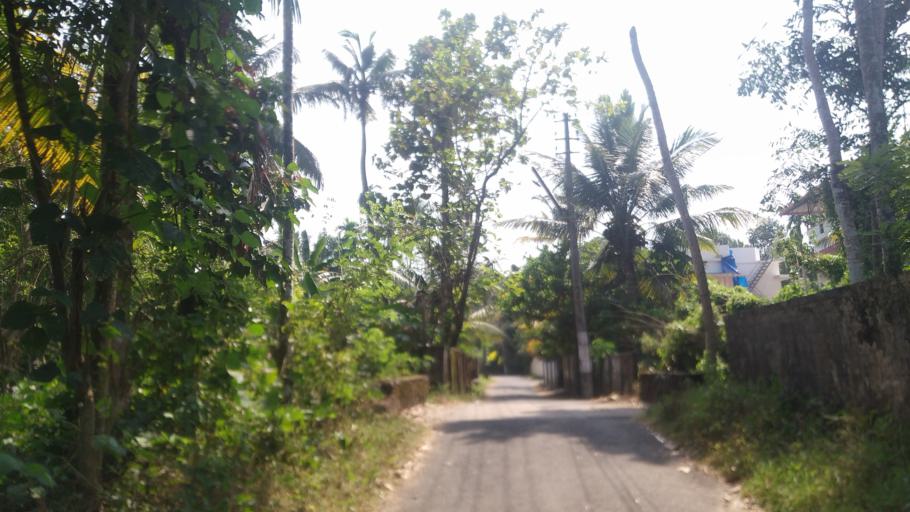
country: IN
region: Kerala
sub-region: Ernakulam
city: Elur
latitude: 10.1256
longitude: 76.2343
